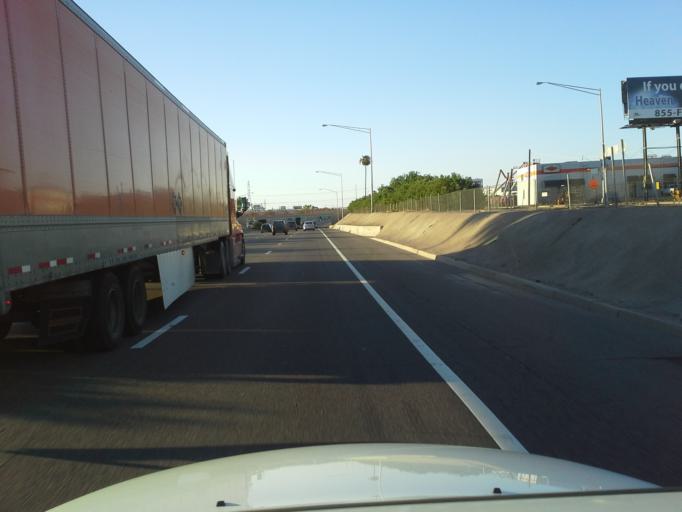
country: US
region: Arizona
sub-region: Maricopa County
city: Phoenix
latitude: 33.4339
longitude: -112.1079
